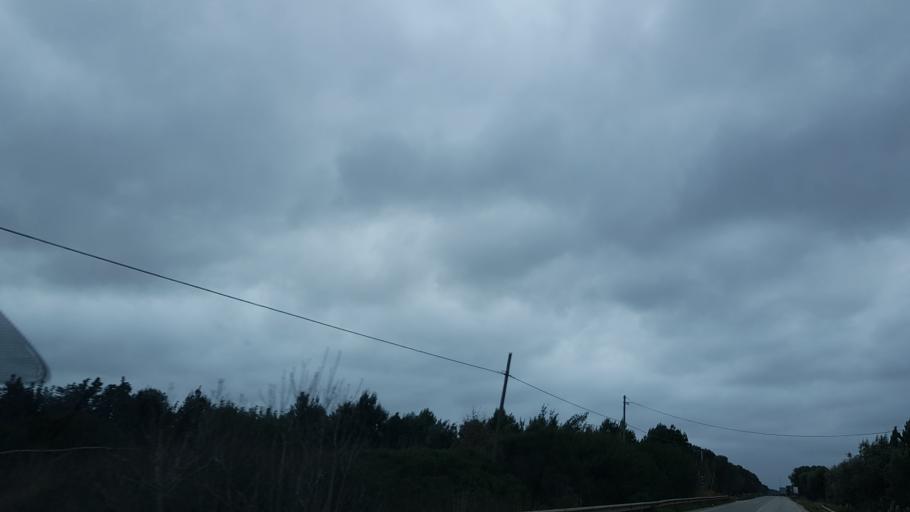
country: IT
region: Apulia
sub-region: Provincia di Brindisi
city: San Vito dei Normanni
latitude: 40.6534
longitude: 17.7859
